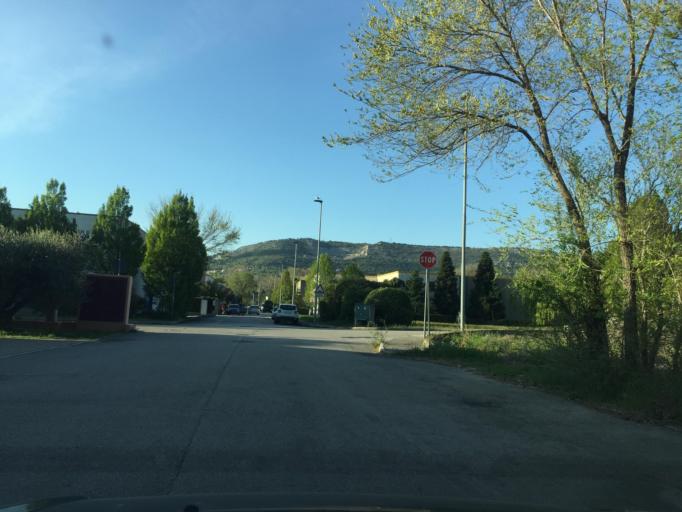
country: IT
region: Friuli Venezia Giulia
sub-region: Provincia di Trieste
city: Dolina
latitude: 45.6030
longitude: 13.8516
